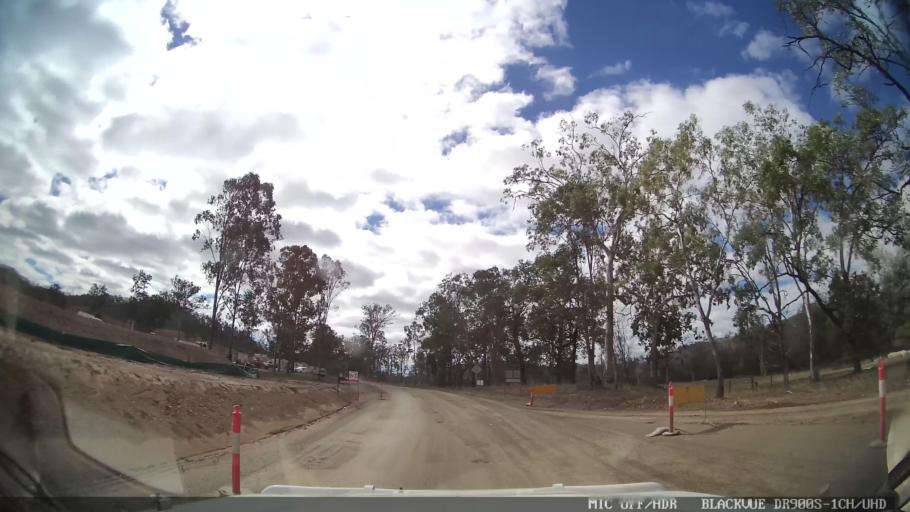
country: AU
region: Queensland
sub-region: Gladstone
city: Toolooa
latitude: -24.6135
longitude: 151.2999
